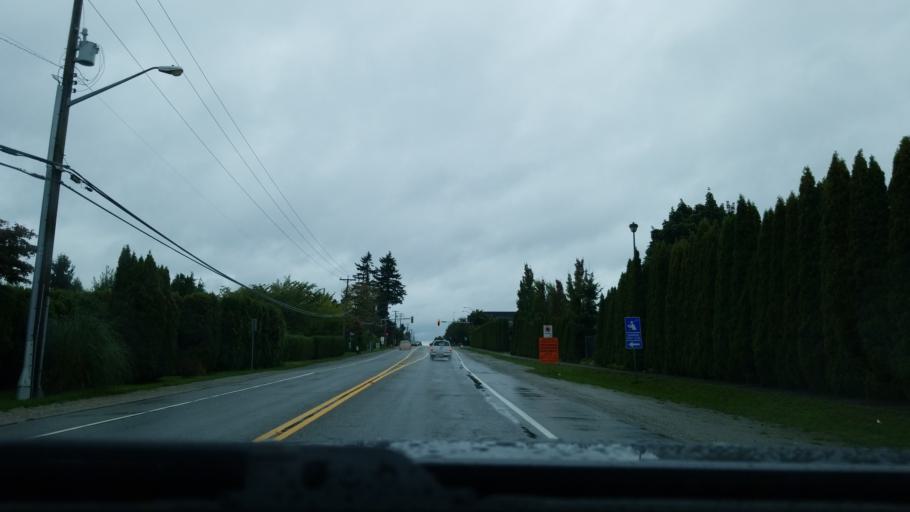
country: CA
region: British Columbia
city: Langley
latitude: 49.1190
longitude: -122.6992
